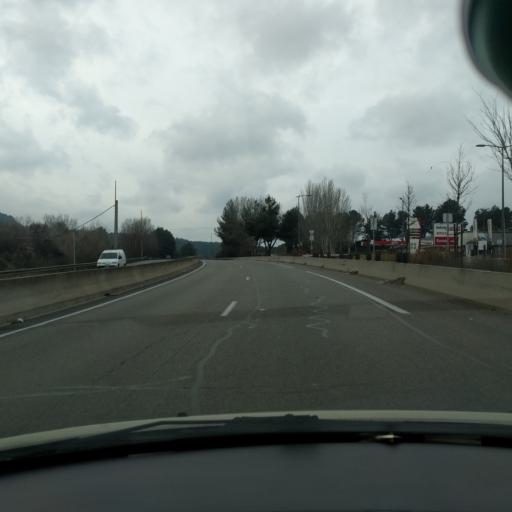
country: FR
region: Provence-Alpes-Cote d'Azur
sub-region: Departement des Bouches-du-Rhone
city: Gardanne
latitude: 43.4534
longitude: 5.4537
